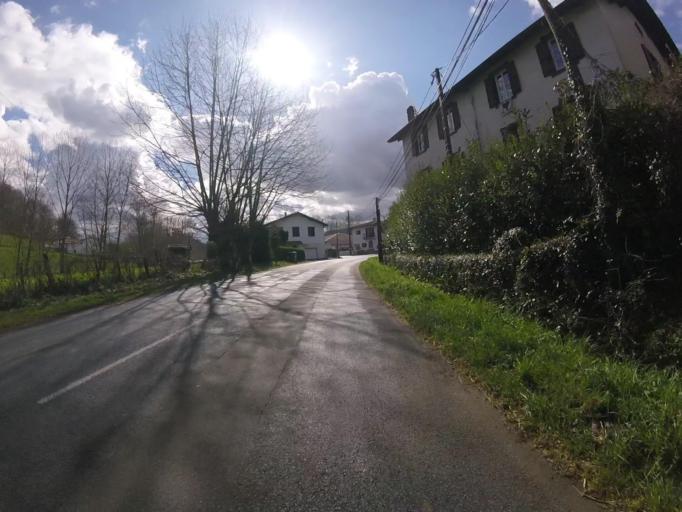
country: FR
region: Aquitaine
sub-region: Departement des Pyrenees-Atlantiques
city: Sare
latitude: 43.3002
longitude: -1.5719
